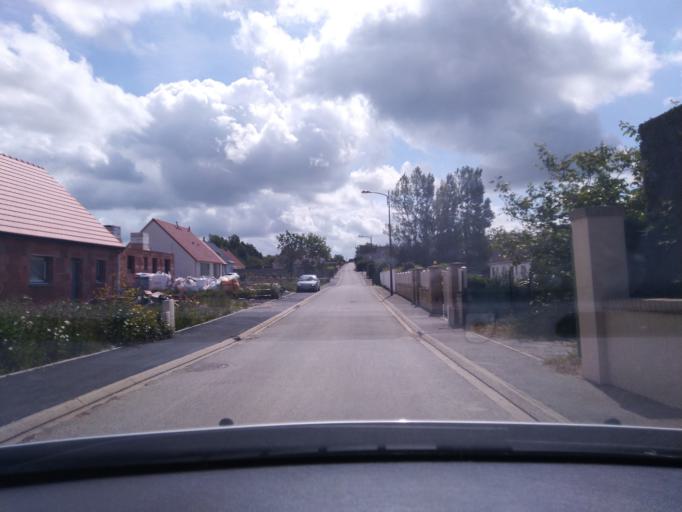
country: FR
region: Nord-Pas-de-Calais
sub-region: Departement du Pas-de-Calais
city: Ferques
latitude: 50.8392
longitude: 1.7601
